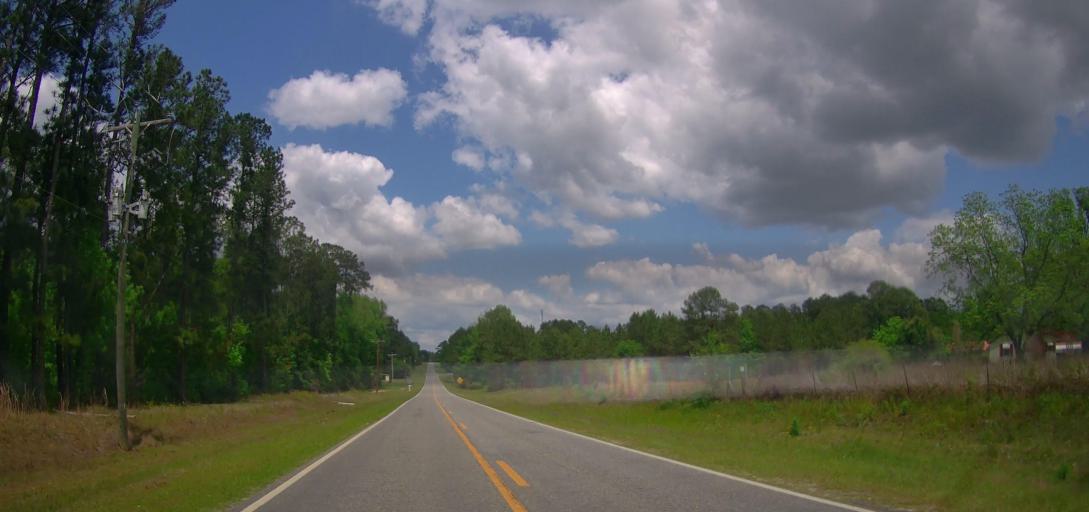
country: US
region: Georgia
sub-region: Laurens County
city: East Dublin
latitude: 32.5687
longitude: -82.8009
